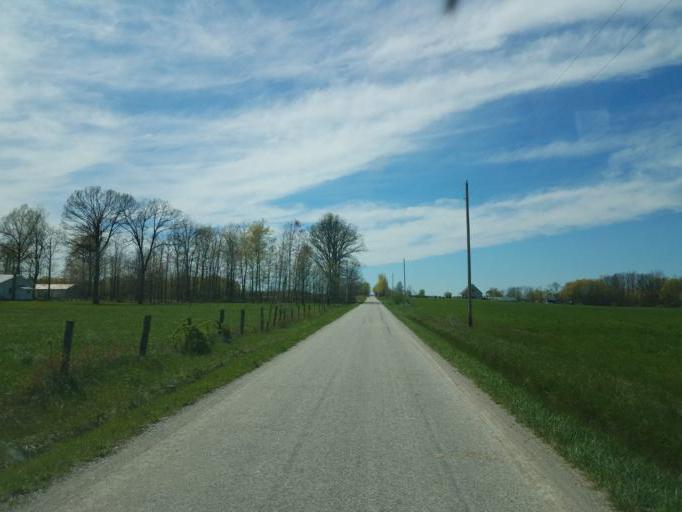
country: US
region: Ohio
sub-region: Ashland County
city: Ashland
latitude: 40.8988
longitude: -82.4081
